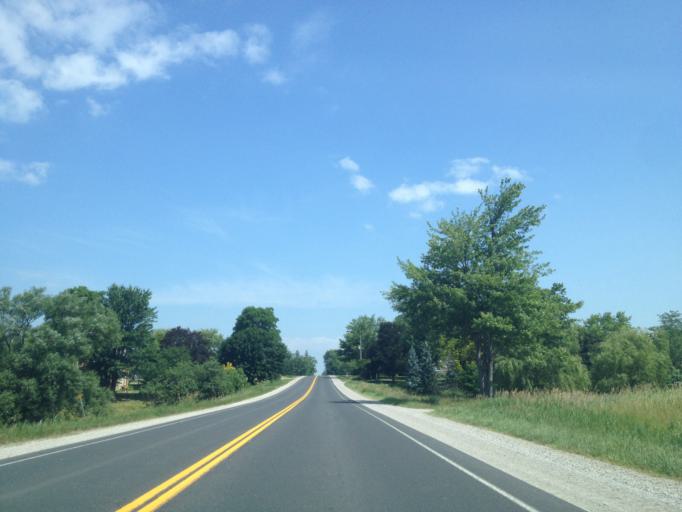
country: CA
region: Ontario
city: Stratford
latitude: 43.3112
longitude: -81.2012
